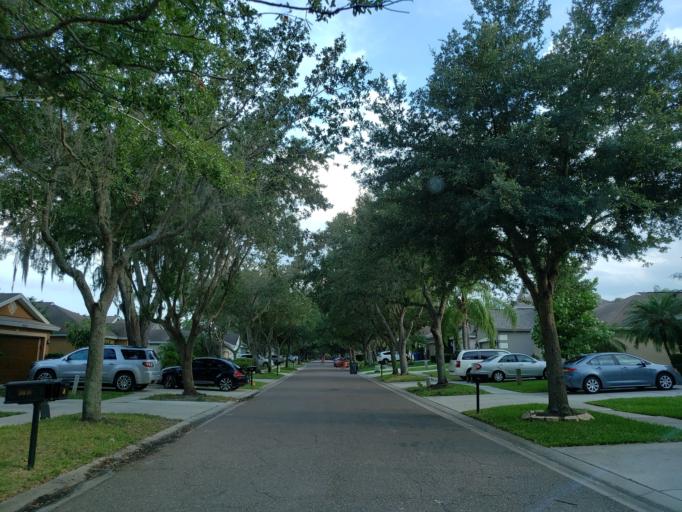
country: US
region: Florida
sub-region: Hillsborough County
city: Fish Hawk
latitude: 27.8491
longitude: -82.2273
